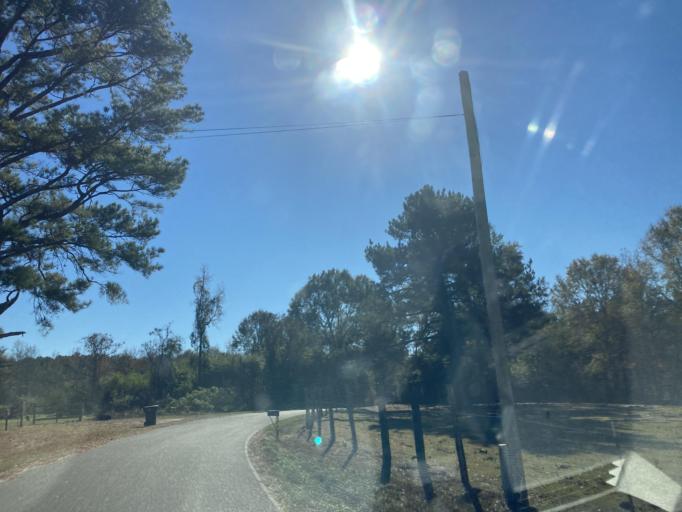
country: US
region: Mississippi
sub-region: Lamar County
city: Sumrall
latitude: 31.2961
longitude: -89.6455
